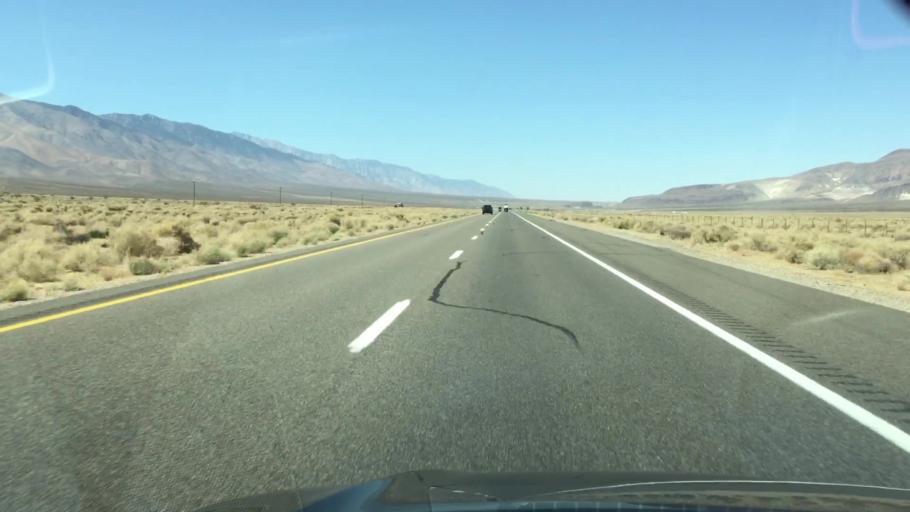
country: US
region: California
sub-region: Kern County
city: Inyokern
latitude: 36.0219
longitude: -117.9396
